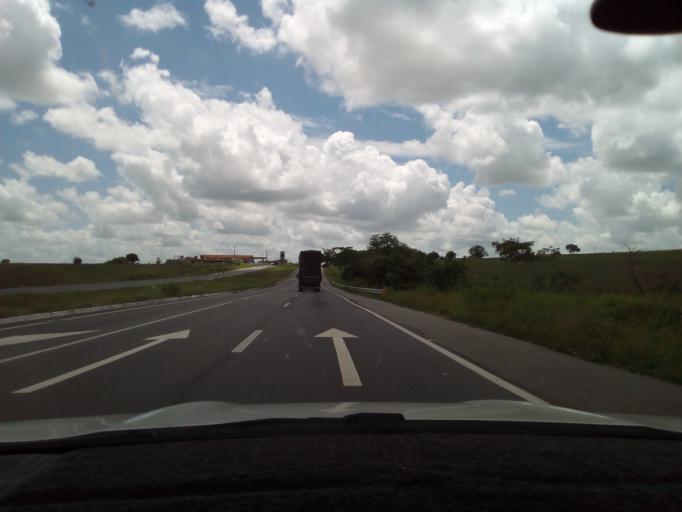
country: BR
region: Paraiba
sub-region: Gurinhem
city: Gurinhem
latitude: -7.1696
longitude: -35.3762
